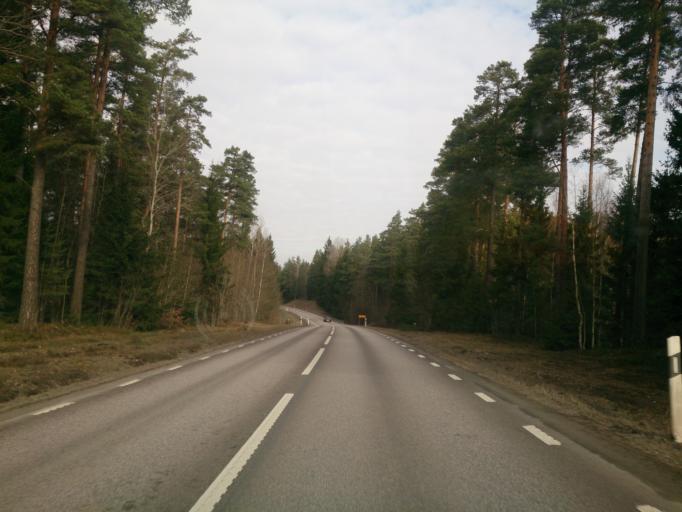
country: SE
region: OEstergoetland
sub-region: Atvidabergs Kommun
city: Atvidaberg
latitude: 58.2660
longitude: 15.9249
